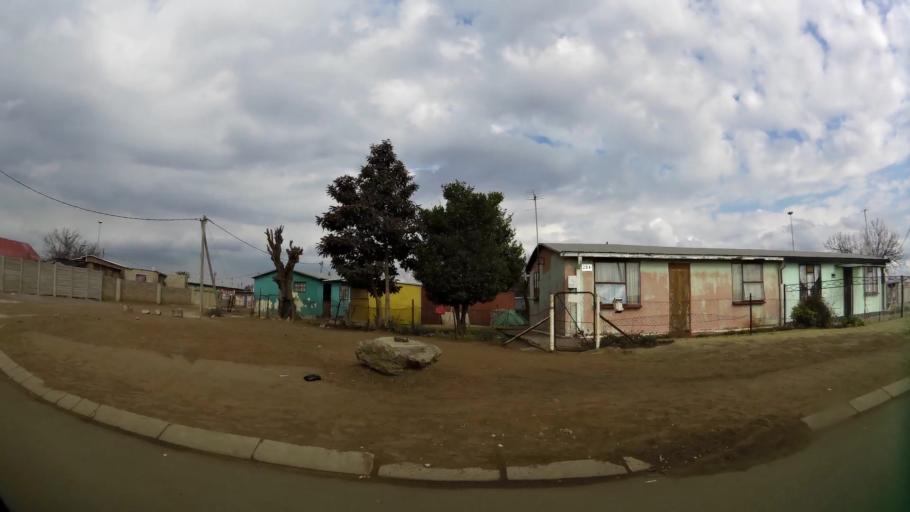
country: ZA
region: Gauteng
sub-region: Sedibeng District Municipality
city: Vanderbijlpark
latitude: -26.6959
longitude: 27.7931
